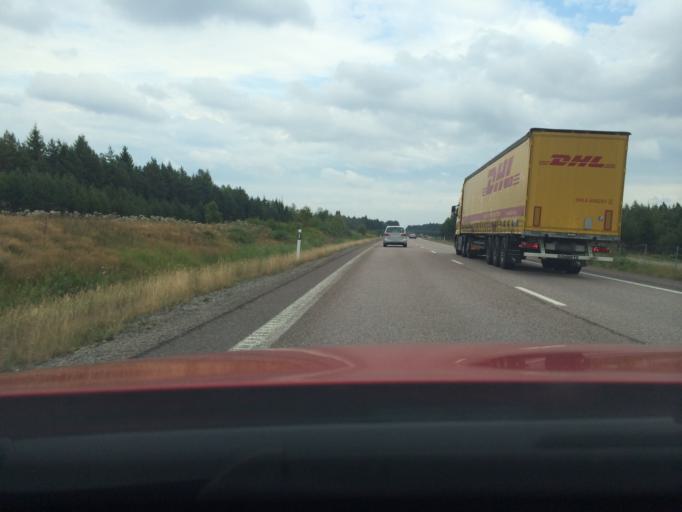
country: SE
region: Soedermanland
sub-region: Nykopings Kommun
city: Stigtomta
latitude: 58.7583
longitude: 16.8052
